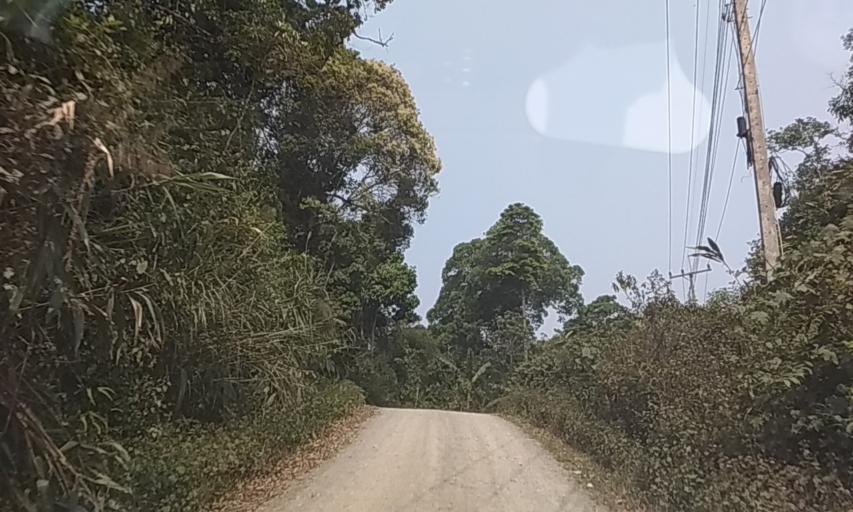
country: TH
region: Nan
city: Chaloem Phra Kiat
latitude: 20.0363
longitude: 101.0946
